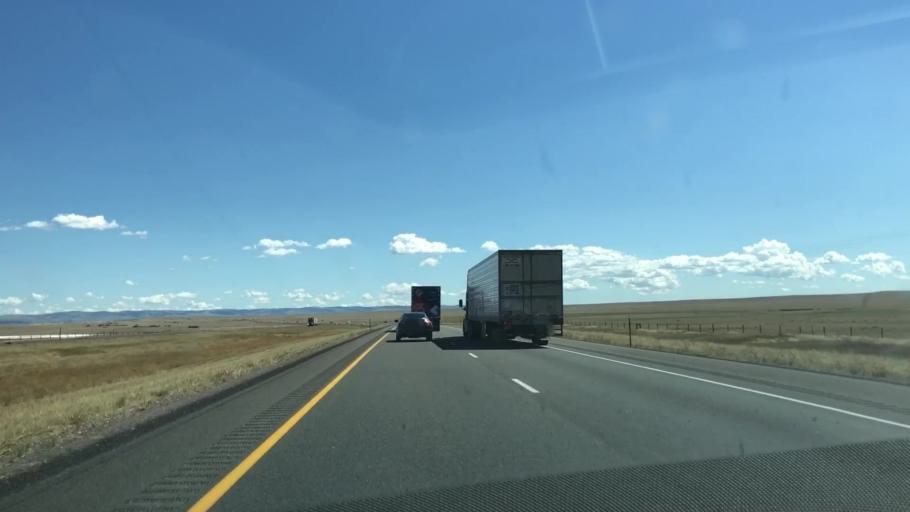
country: US
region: Wyoming
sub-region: Albany County
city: Laramie
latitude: 41.3711
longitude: -105.7919
